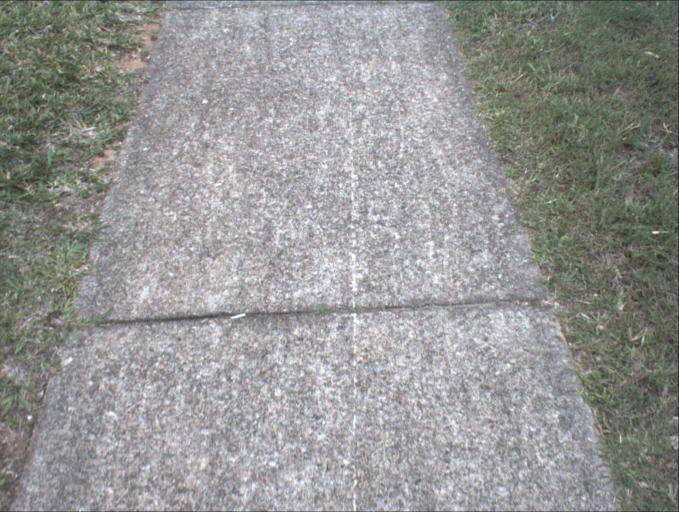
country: AU
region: Queensland
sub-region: Logan
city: Park Ridge South
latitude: -27.6789
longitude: 153.0192
